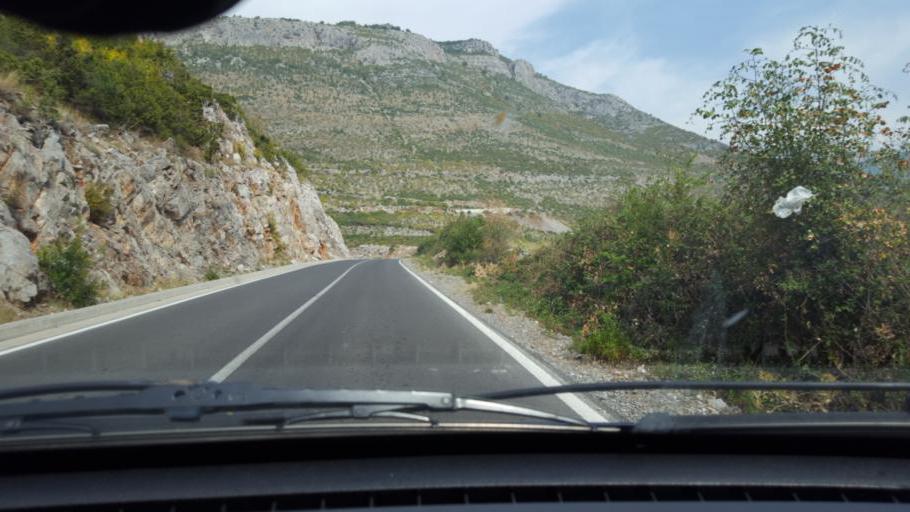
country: AL
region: Shkoder
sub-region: Rrethi i Malesia e Madhe
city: Hot
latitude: 42.3699
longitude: 19.4498
